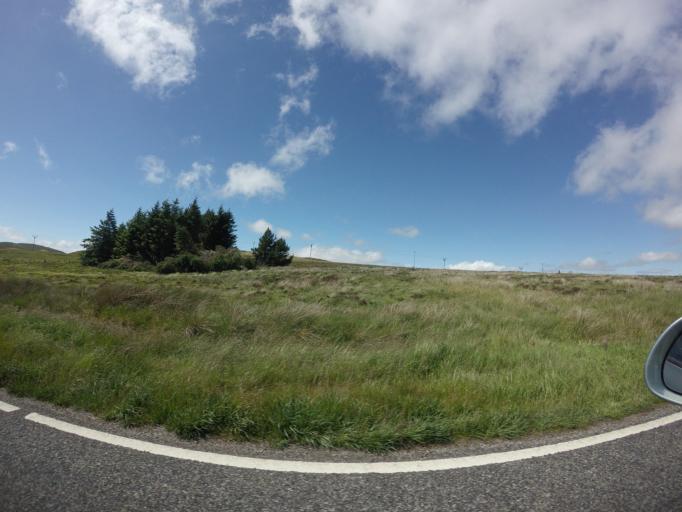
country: GB
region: Scotland
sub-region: Eilean Siar
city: Stornoway
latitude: 58.1481
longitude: -6.5058
